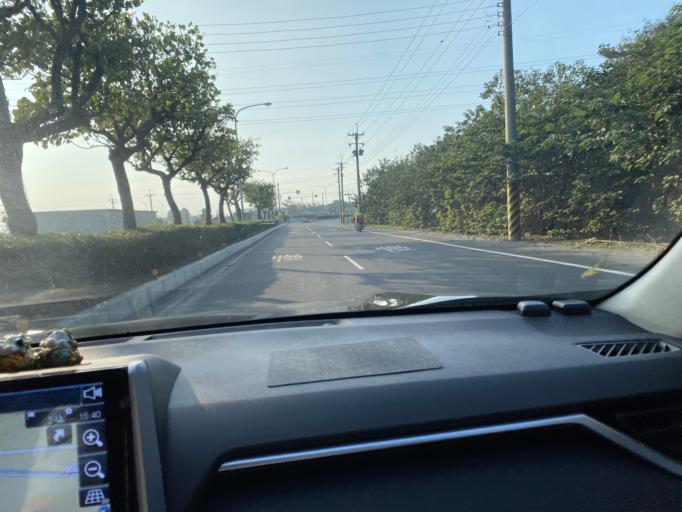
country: TW
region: Taiwan
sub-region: Changhua
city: Chang-hua
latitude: 23.9601
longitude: 120.3622
